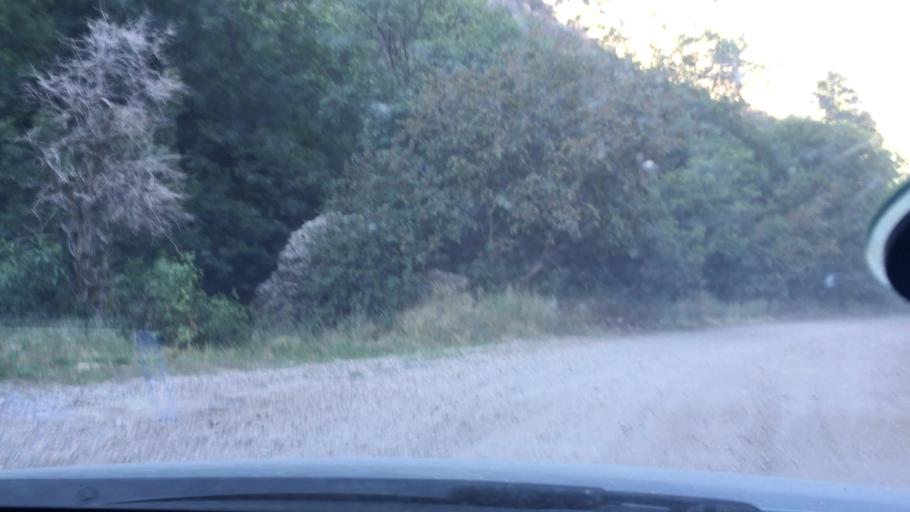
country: US
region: Utah
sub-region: Sanpete County
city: Fountain Green
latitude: 39.5553
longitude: -111.6701
